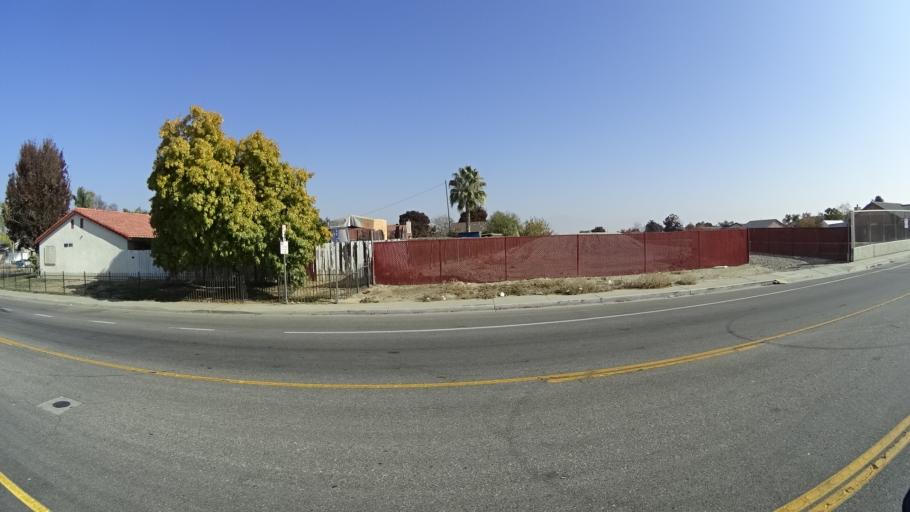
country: US
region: California
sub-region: Kern County
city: Greenfield
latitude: 35.2927
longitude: -119.0120
